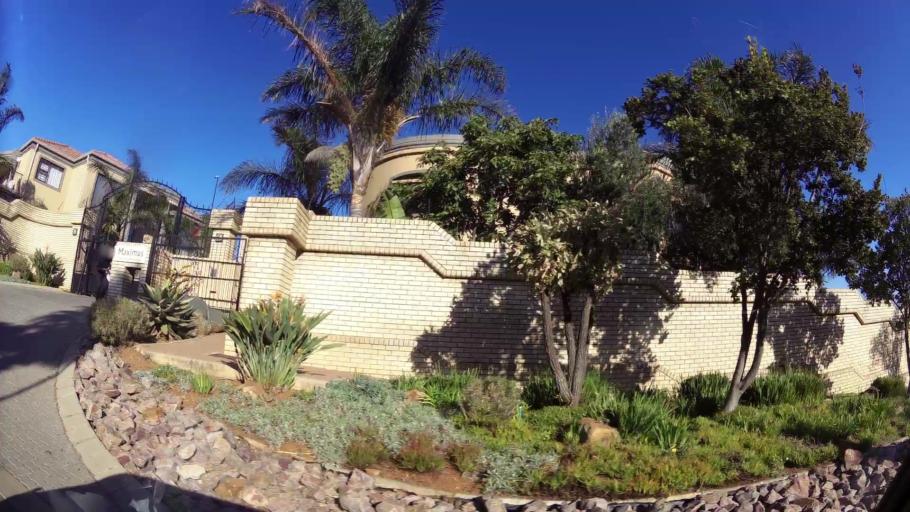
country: ZA
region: Gauteng
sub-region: City of Johannesburg Metropolitan Municipality
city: Johannesburg
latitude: -26.2712
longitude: 28.0537
